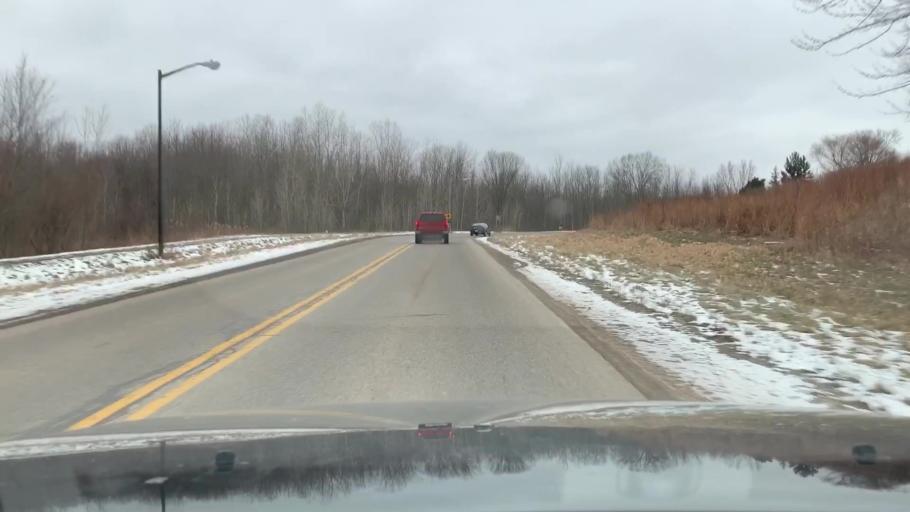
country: US
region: Michigan
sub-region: Ottawa County
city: Zeeland
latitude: 42.7848
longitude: -86.0369
